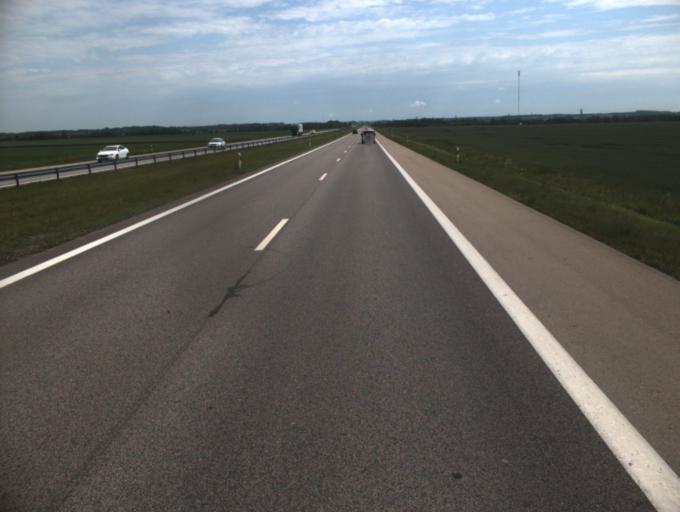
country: LT
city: Raseiniai
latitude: 55.3320
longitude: 23.1223
